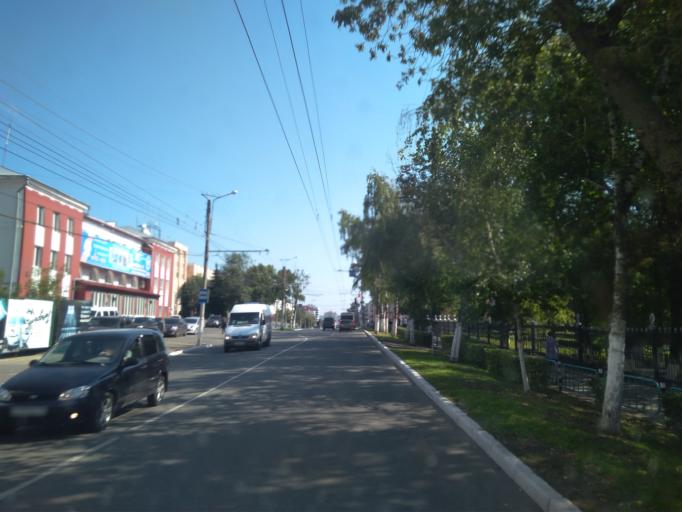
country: RU
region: Mordoviya
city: Saransk
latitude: 54.1848
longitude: 45.1697
